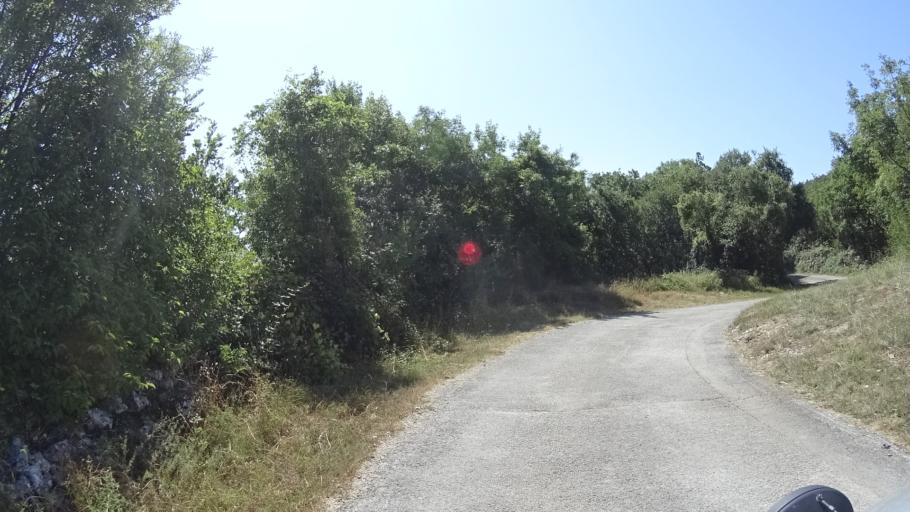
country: HR
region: Istarska
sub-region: Grad Labin
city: Rabac
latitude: 44.9903
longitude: 14.1520
